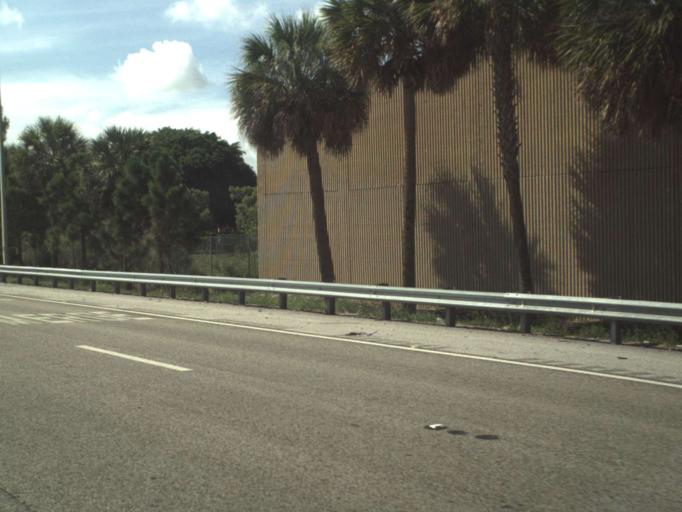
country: US
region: Florida
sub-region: Palm Beach County
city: Schall Circle
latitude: 26.7147
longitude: -80.0851
